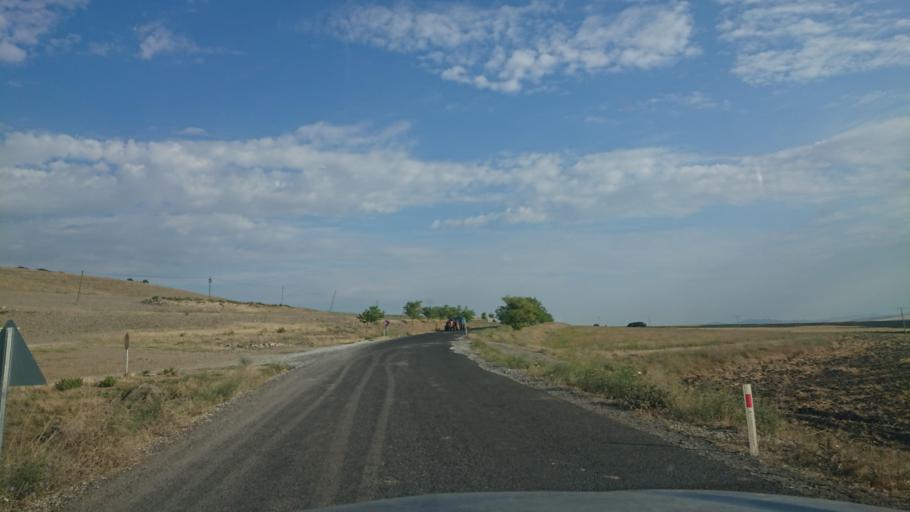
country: TR
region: Aksaray
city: Ortakoy
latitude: 38.8000
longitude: 34.0640
